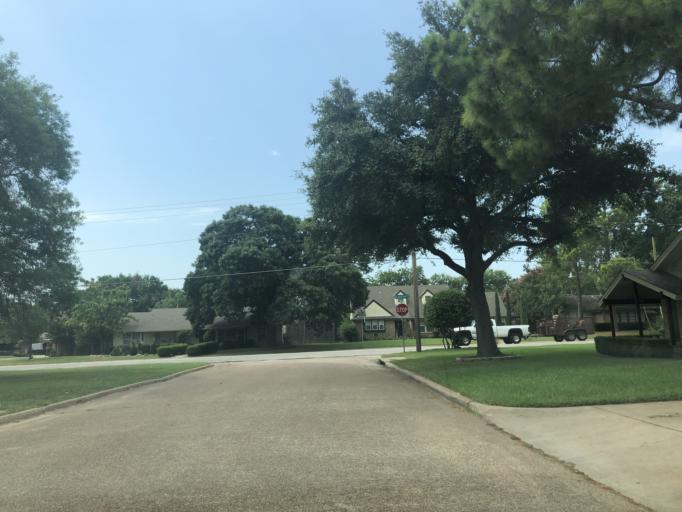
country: US
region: Texas
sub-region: Dallas County
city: Grand Prairie
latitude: 32.7648
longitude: -97.0174
